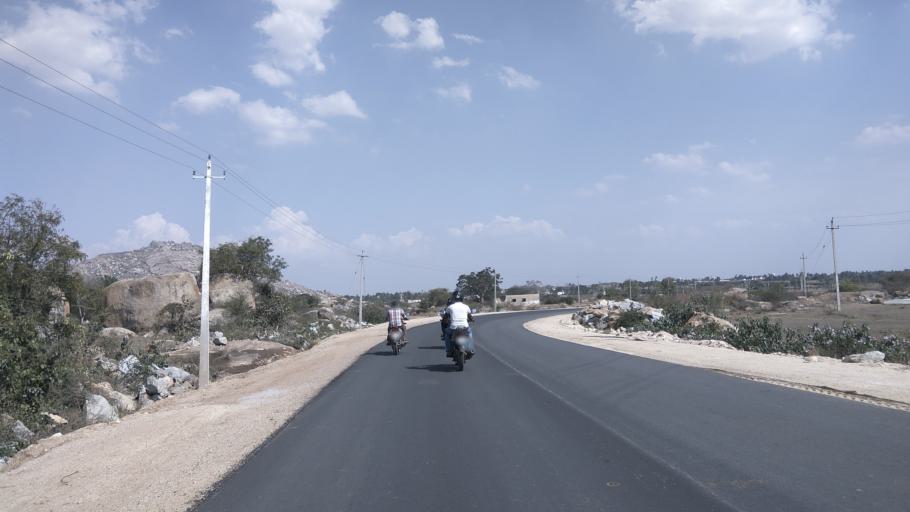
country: IN
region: Karnataka
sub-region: Kolar
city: Mulbagal
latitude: 13.1750
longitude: 78.3554
